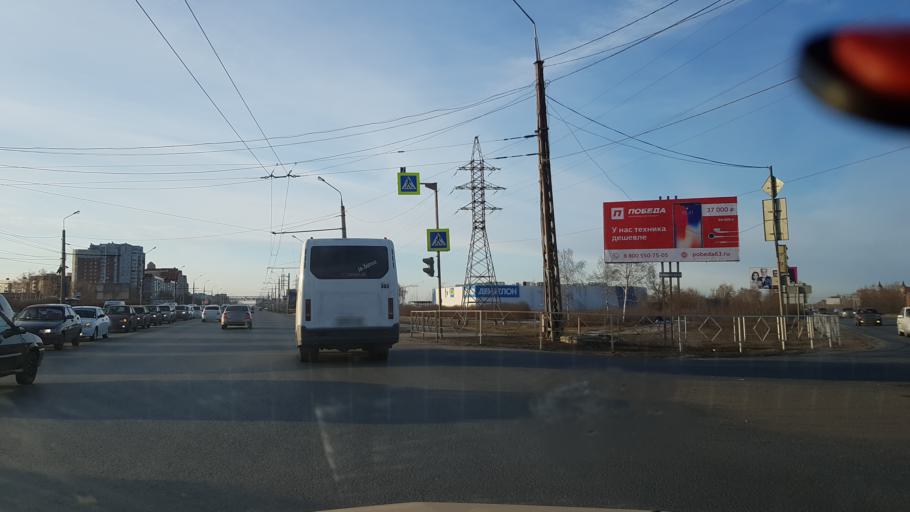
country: RU
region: Samara
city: Tol'yatti
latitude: 53.5452
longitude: 49.3802
